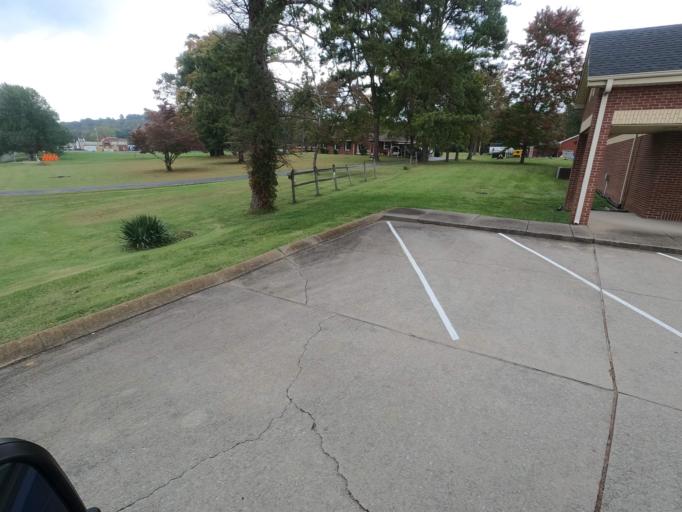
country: US
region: Tennessee
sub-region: Cheatham County
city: Pegram
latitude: 36.1018
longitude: -87.0531
